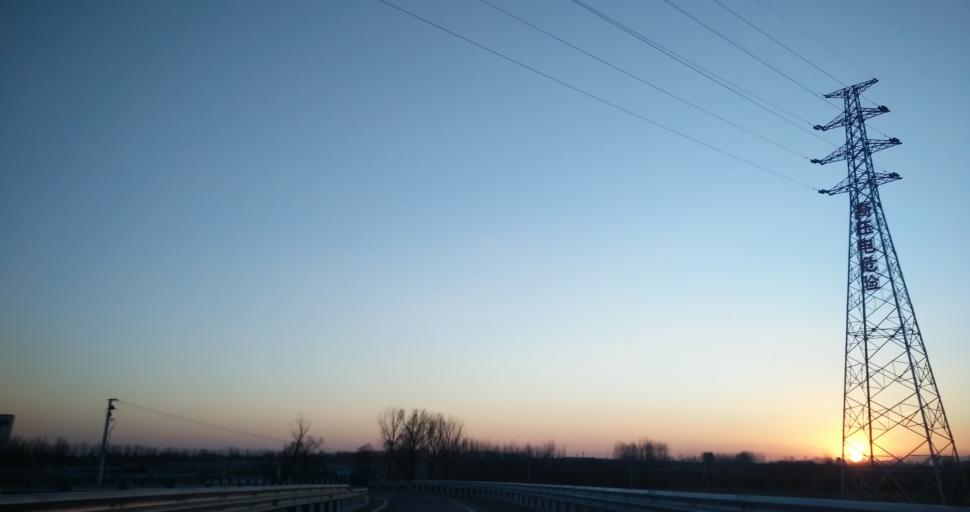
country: CN
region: Beijing
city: Qingyundian
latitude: 39.6811
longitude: 116.4484
